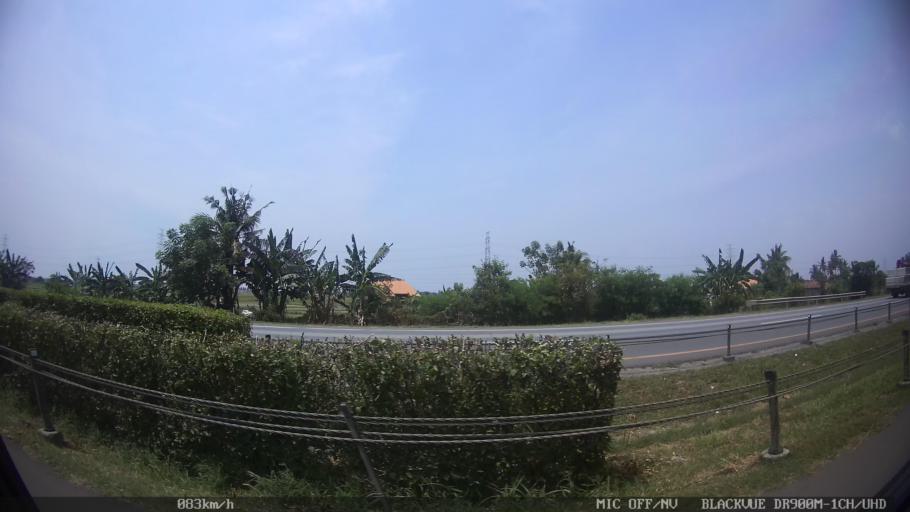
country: ID
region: Banten
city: Serang
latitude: -6.0536
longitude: 106.1188
